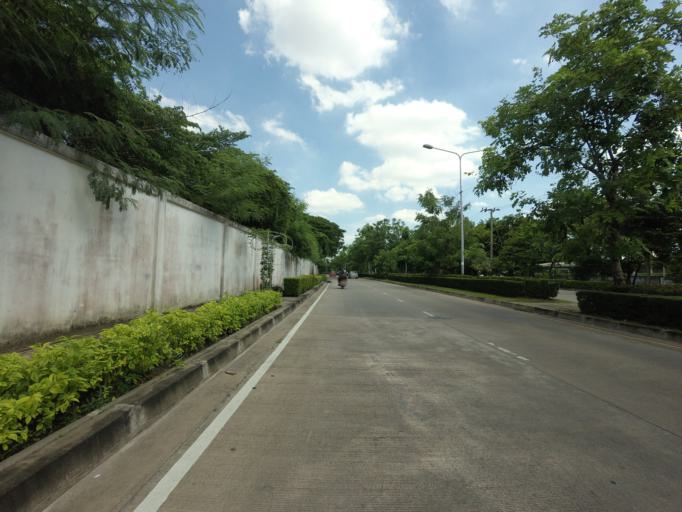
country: TH
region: Bangkok
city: Chatuchak
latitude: 13.8475
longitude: 100.5890
